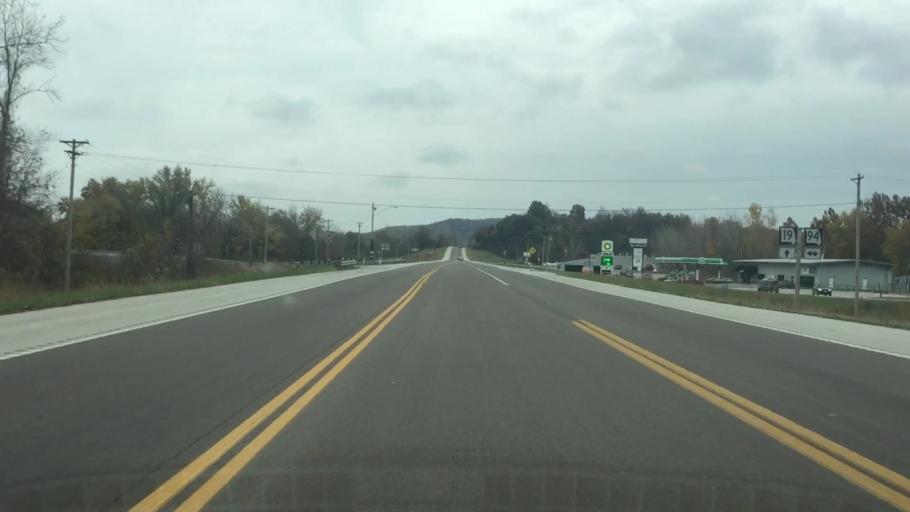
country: US
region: Missouri
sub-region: Gasconade County
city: Hermann
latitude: 38.7280
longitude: -91.4459
